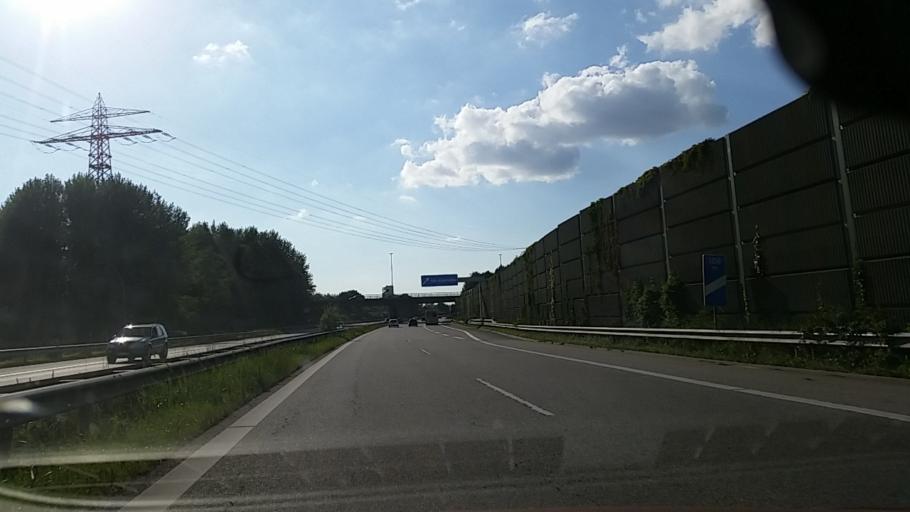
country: DE
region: Schleswig-Holstein
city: Oststeinbek
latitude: 53.4861
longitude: 10.1186
